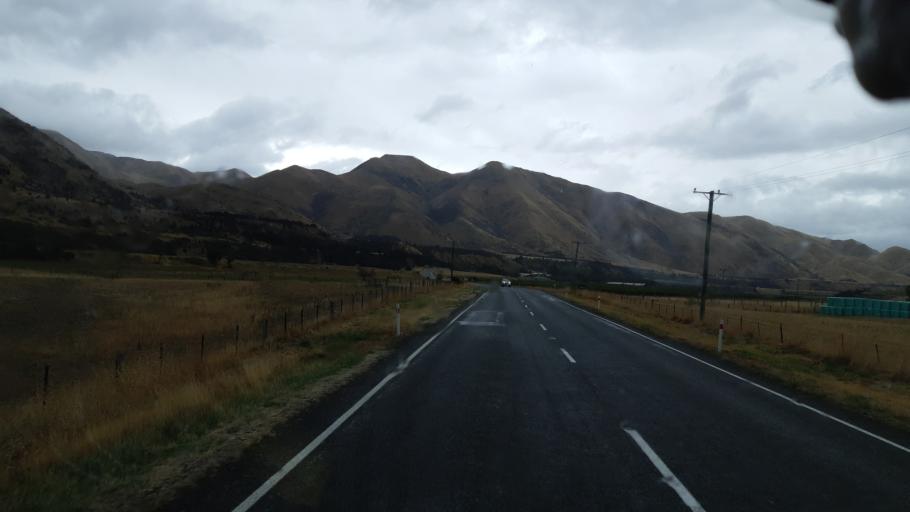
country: NZ
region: Canterbury
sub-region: Hurunui District
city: Amberley
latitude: -42.6261
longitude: 172.7666
